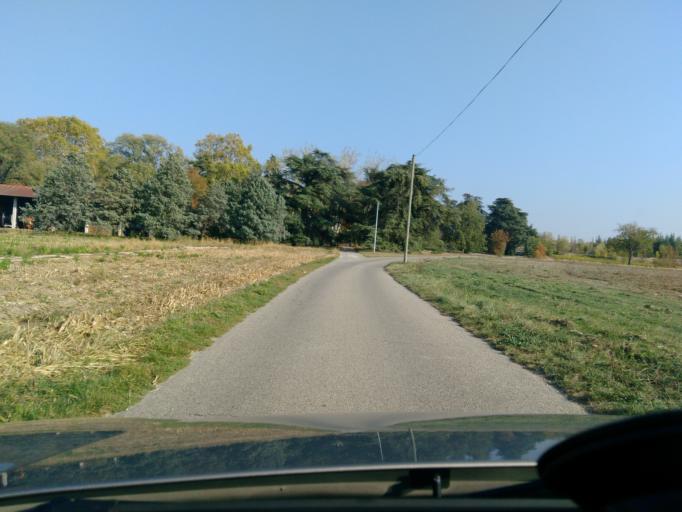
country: FR
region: Rhone-Alpes
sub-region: Departement de la Drome
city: Montboucher-sur-Jabron
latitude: 44.5413
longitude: 4.8115
